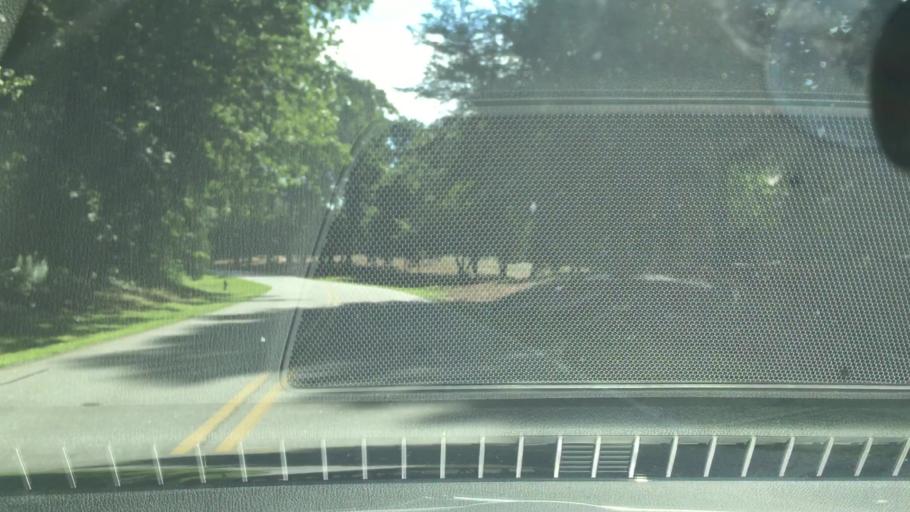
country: US
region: Georgia
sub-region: Putnam County
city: Jefferson
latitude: 33.3878
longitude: -83.2462
